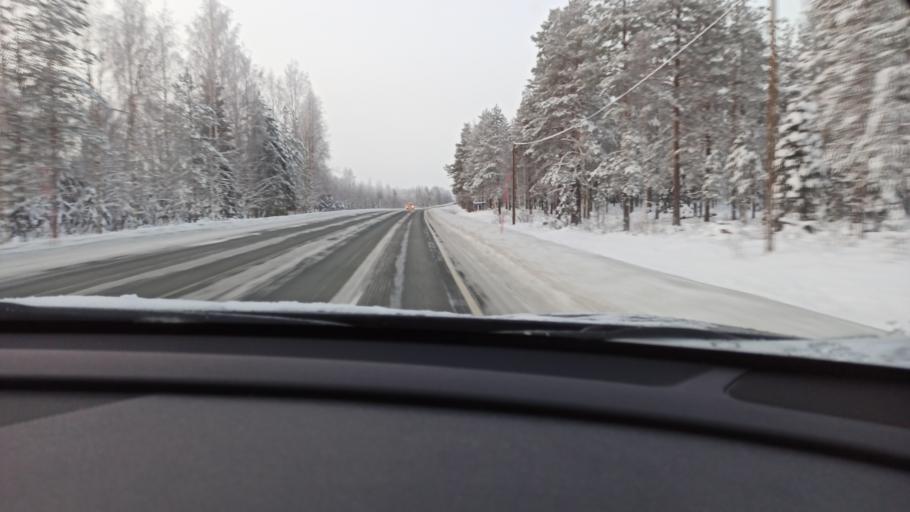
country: FI
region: Lapland
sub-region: Rovaniemi
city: Rovaniemi
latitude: 66.5501
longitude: 25.8855
